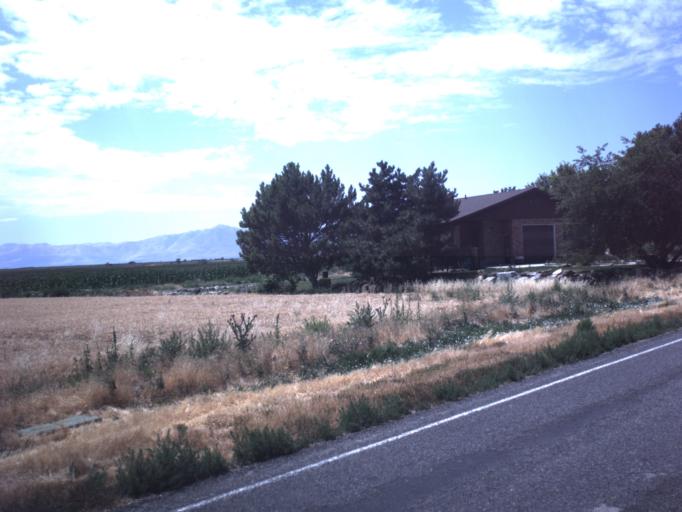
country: US
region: Utah
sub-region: Box Elder County
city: Tremonton
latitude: 41.6509
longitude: -112.2993
